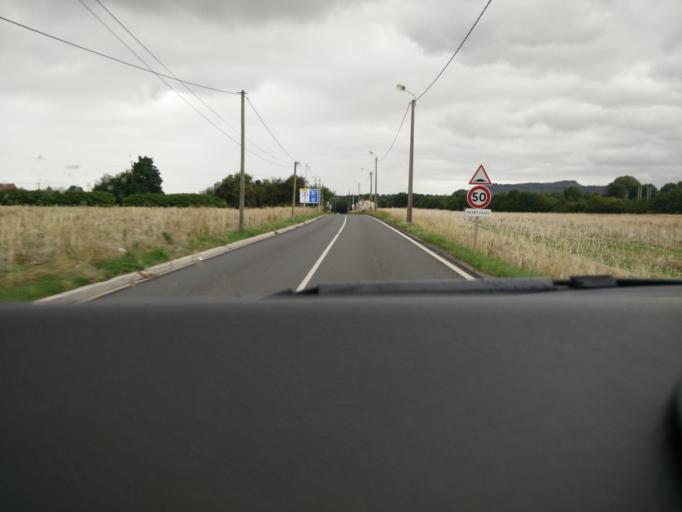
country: FR
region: Nord-Pas-de-Calais
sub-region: Departement du Pas-de-Calais
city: Grenay
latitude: 50.4420
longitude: 2.7437
